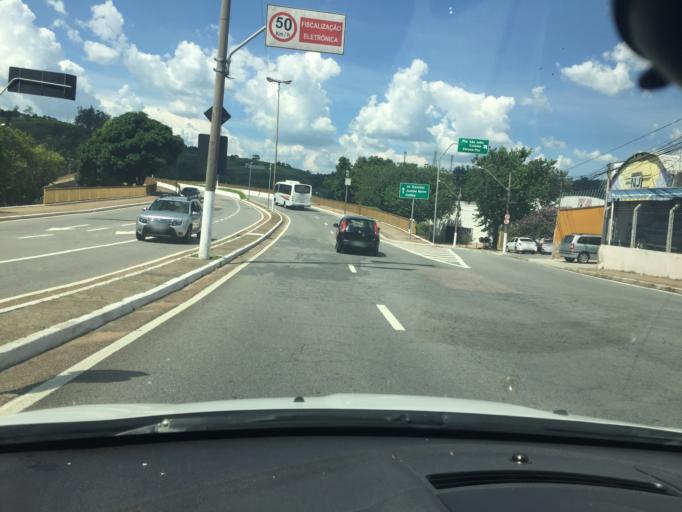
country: BR
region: Sao Paulo
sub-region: Jundiai
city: Jundiai
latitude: -23.1749
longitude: -46.8863
